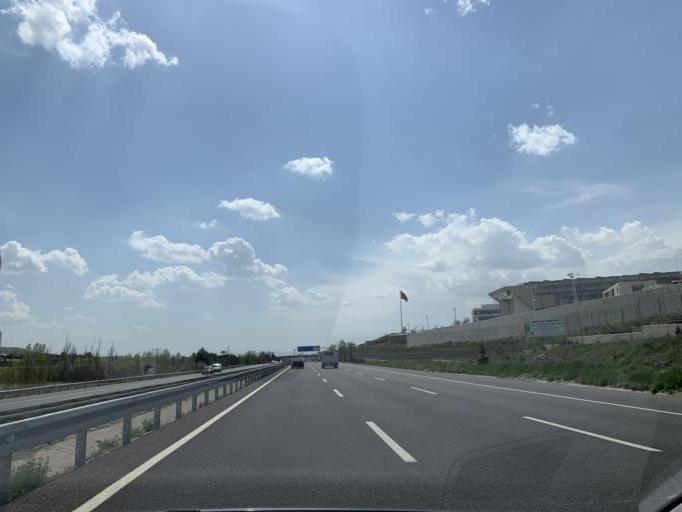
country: TR
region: Ankara
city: Etimesgut
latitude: 39.8197
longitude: 32.5677
